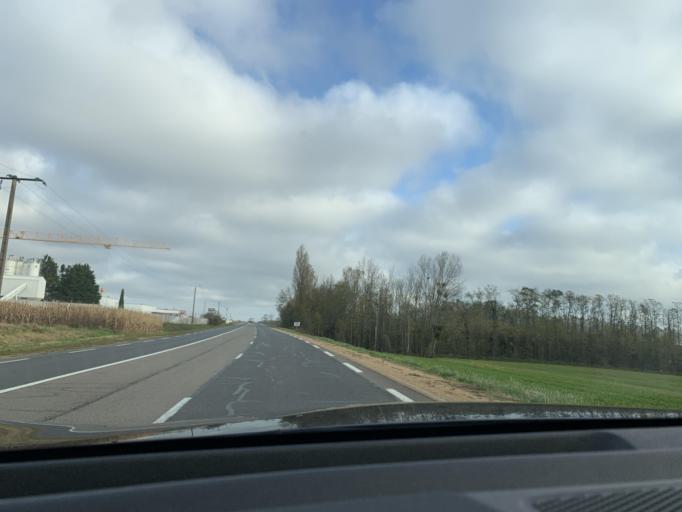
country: FR
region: Bourgogne
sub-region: Departement de Saone-et-Loire
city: Saint-Martin-Belle-Roche
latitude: 46.3900
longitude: 4.8732
